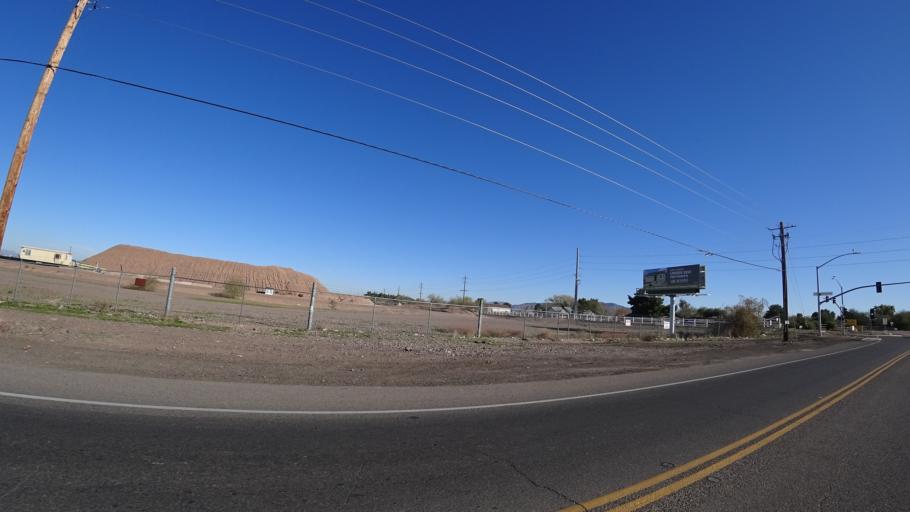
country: US
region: Arizona
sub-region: Maricopa County
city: Laveen
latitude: 33.3926
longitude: -112.2029
